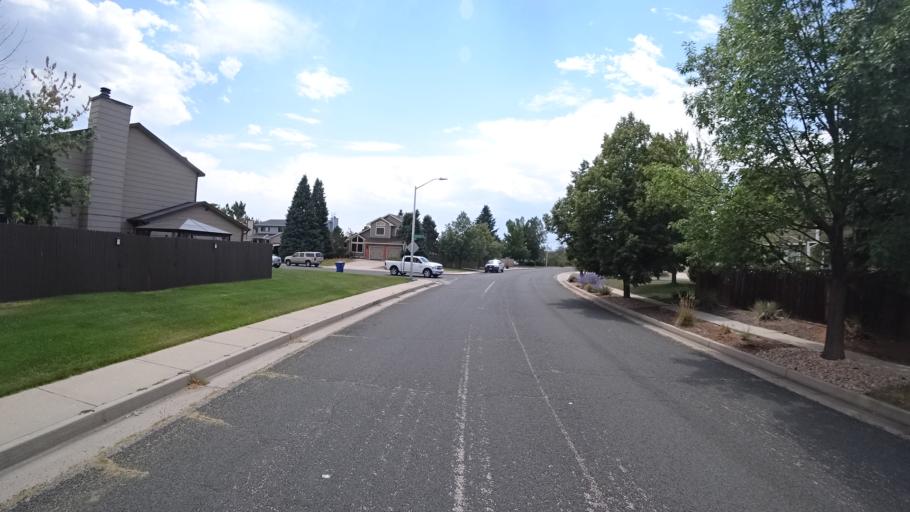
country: US
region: Colorado
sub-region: El Paso County
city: Black Forest
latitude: 38.9598
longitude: -104.7556
